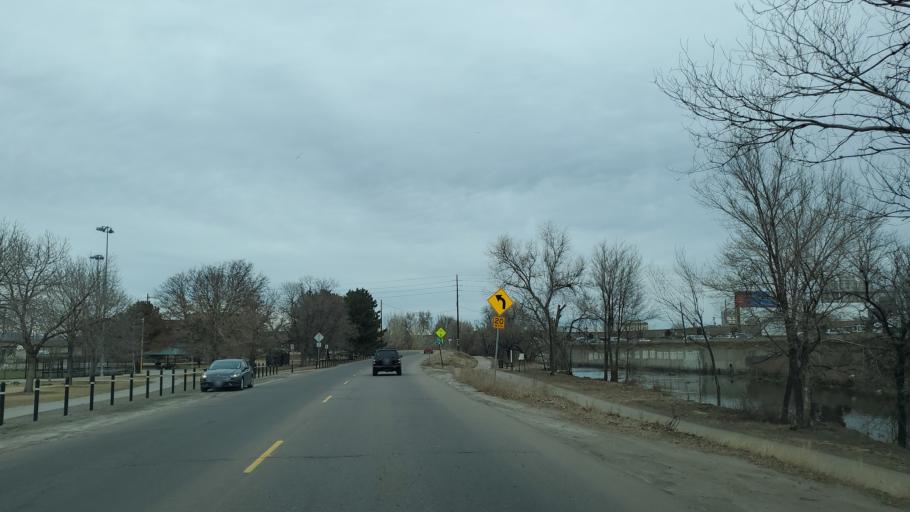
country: US
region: Colorado
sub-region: Denver County
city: Denver
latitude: 39.7132
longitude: -105.0016
